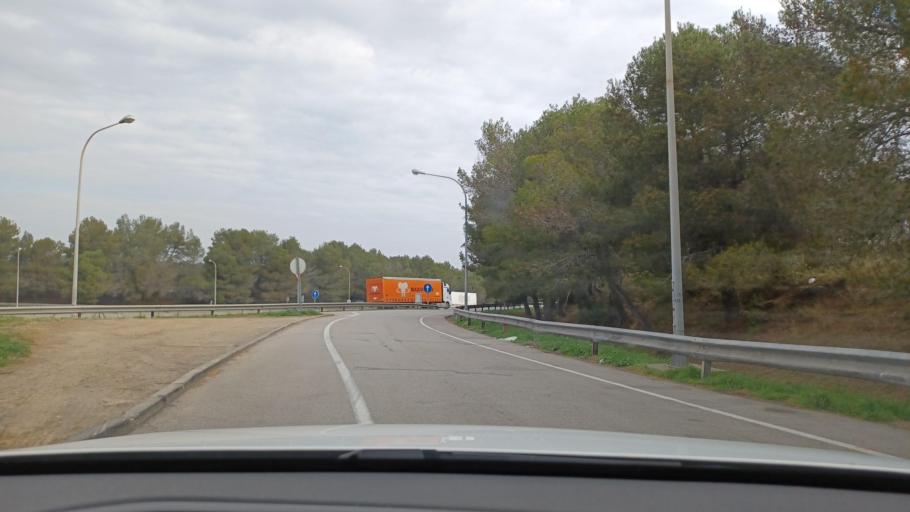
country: ES
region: Catalonia
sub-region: Provincia de Tarragona
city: Sant Jaume dels Domenys
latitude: 41.2892
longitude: 1.5941
